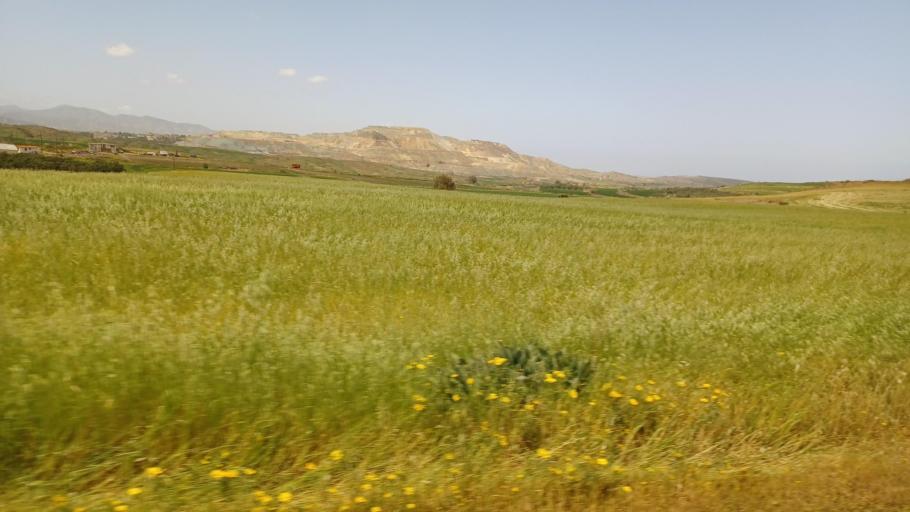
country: CY
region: Lefkosia
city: Lefka
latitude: 35.0821
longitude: 32.9259
